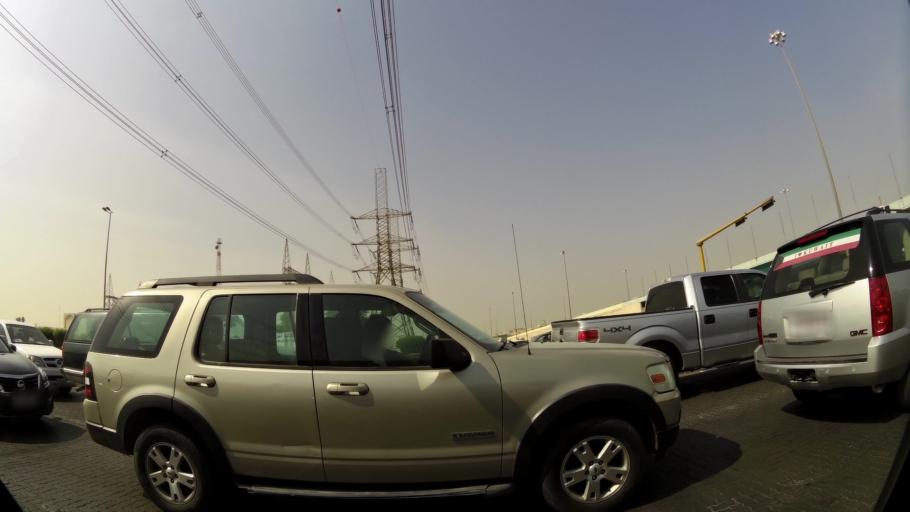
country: KW
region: Al Asimah
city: Ar Rabiyah
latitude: 29.3000
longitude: 47.9277
